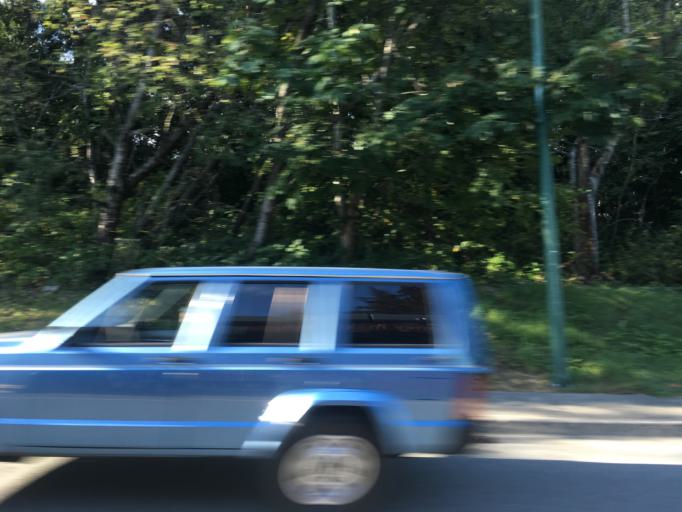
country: CA
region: British Columbia
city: Port Moody
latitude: 49.2436
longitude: -122.8179
